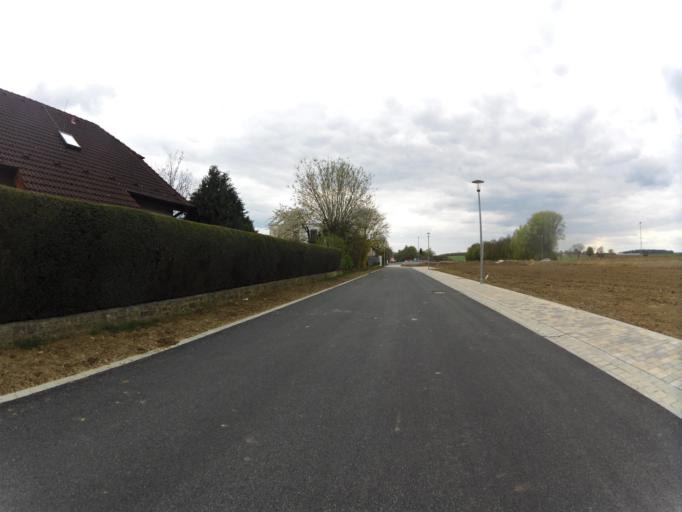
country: DE
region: Bavaria
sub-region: Regierungsbezirk Unterfranken
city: Giebelstadt
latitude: 49.6565
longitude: 9.9420
